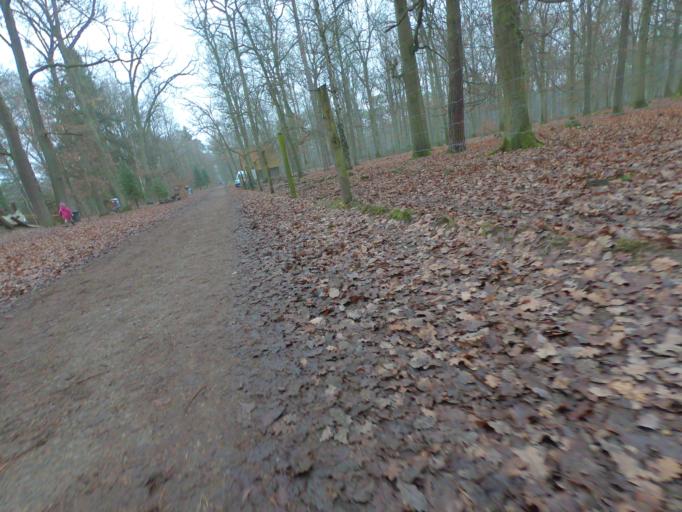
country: DE
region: Hesse
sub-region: Regierungsbezirk Darmstadt
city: Hanau am Main
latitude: 50.0804
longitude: 8.9095
